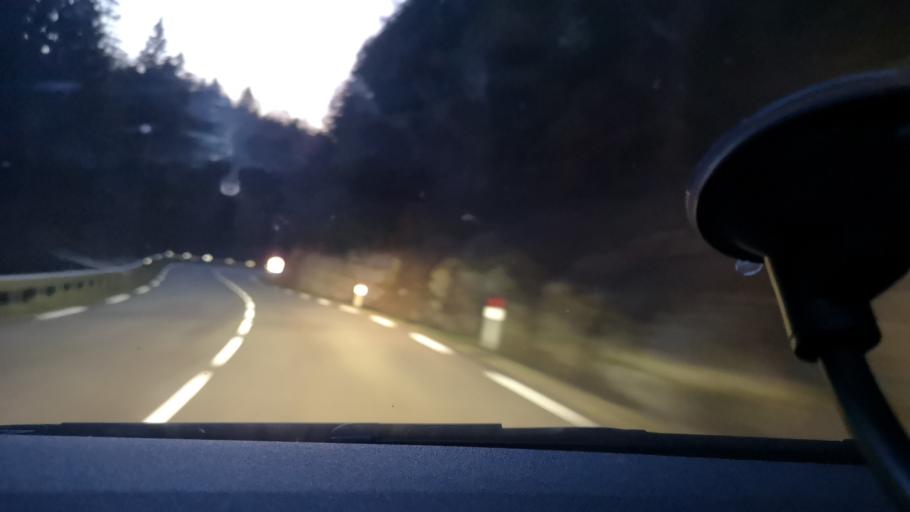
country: FR
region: Franche-Comte
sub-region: Departement du Jura
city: Champagnole
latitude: 46.7577
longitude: 5.9647
